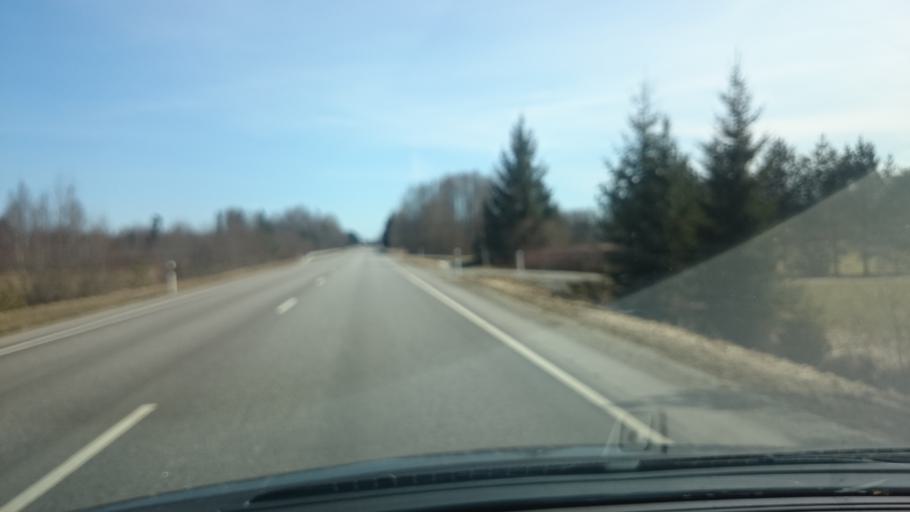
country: EE
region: Paernumaa
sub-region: Vaendra vald (alev)
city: Vandra
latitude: 58.6693
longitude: 25.1374
